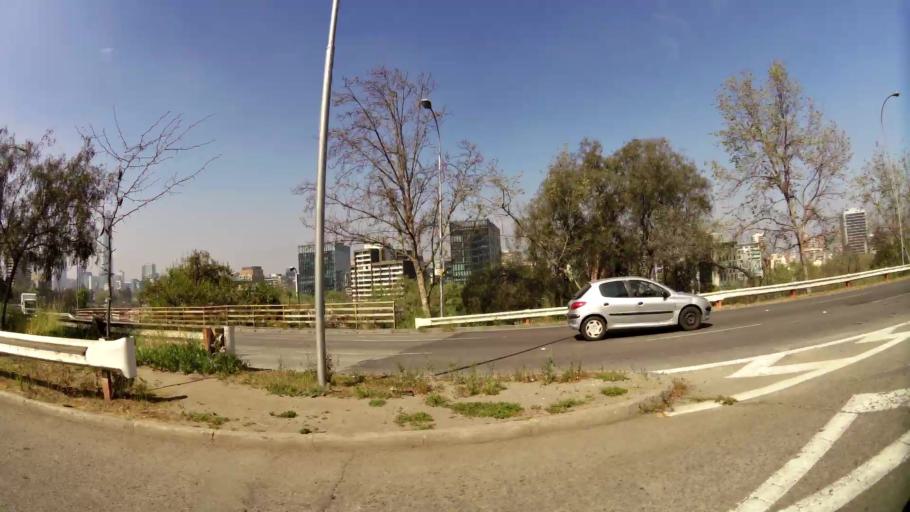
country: CL
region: Santiago Metropolitan
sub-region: Provincia de Santiago
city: Santiago
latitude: -33.4245
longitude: -70.6233
